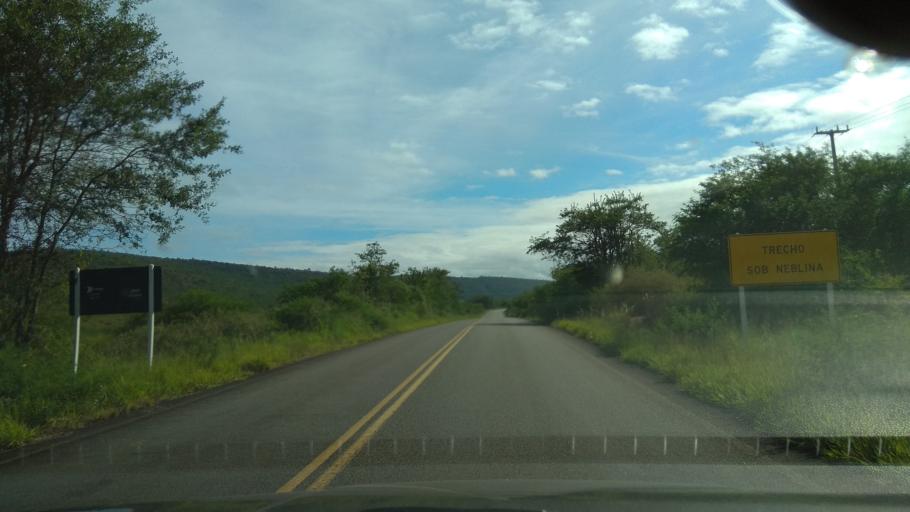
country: BR
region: Bahia
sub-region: Santa Ines
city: Santa Ines
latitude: -13.3657
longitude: -39.8831
